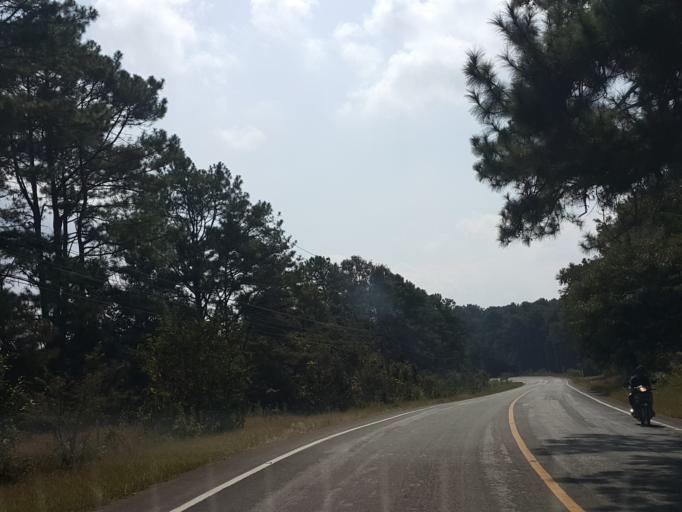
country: TH
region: Chiang Mai
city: Hot
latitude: 18.1290
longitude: 98.3762
